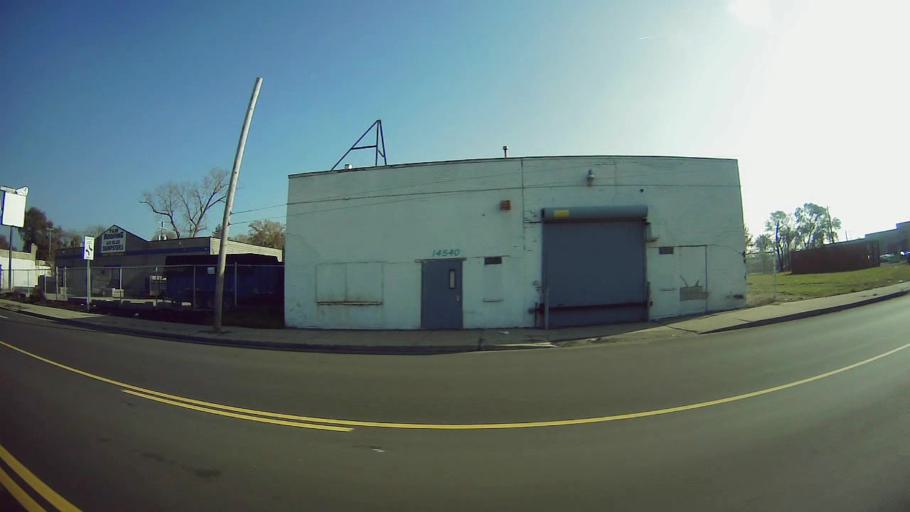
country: US
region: Michigan
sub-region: Oakland County
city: Oak Park
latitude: 42.3954
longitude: -83.1789
